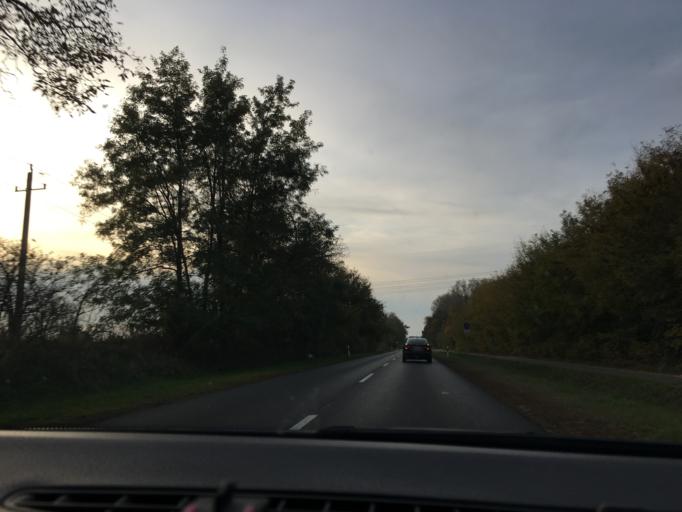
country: HU
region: Szabolcs-Szatmar-Bereg
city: Kallosemjen
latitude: 47.8625
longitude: 21.8897
